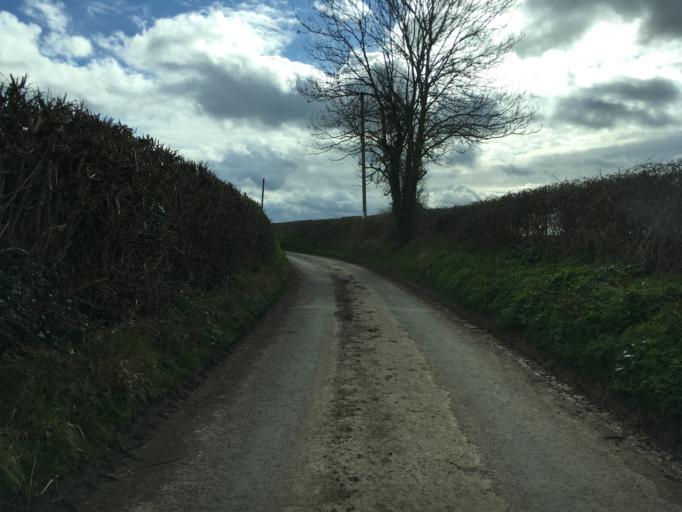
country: GB
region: England
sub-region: Gloucestershire
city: Newent
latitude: 51.8483
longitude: -2.3862
